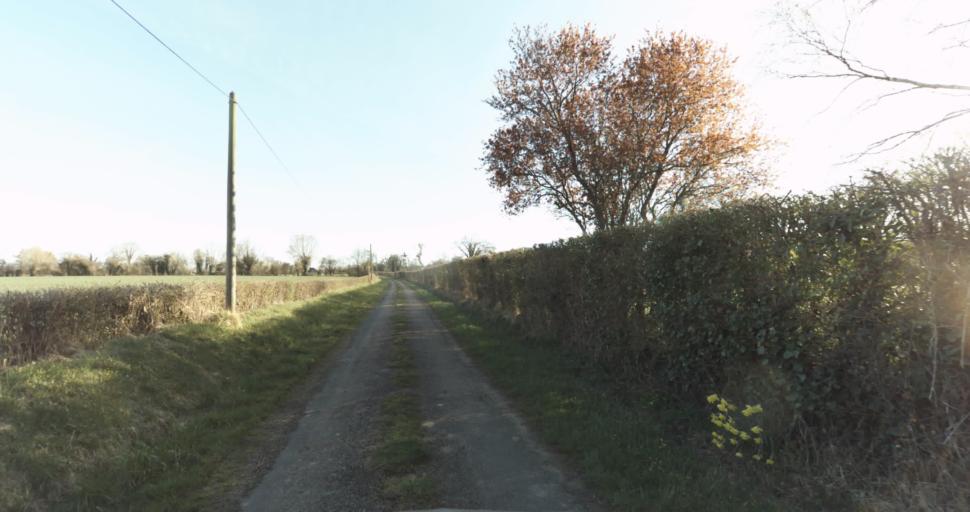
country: FR
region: Lower Normandy
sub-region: Departement de l'Orne
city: Trun
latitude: 48.9141
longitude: 0.0166
